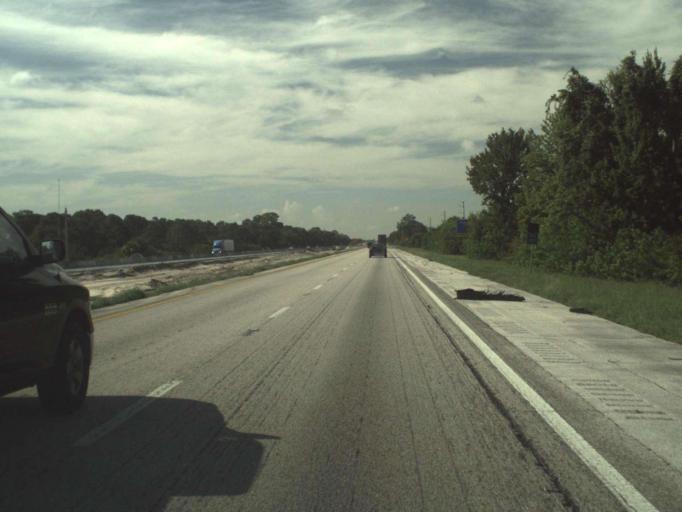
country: US
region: Florida
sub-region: Indian River County
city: West Vero Corridor
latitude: 27.6999
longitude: -80.5400
